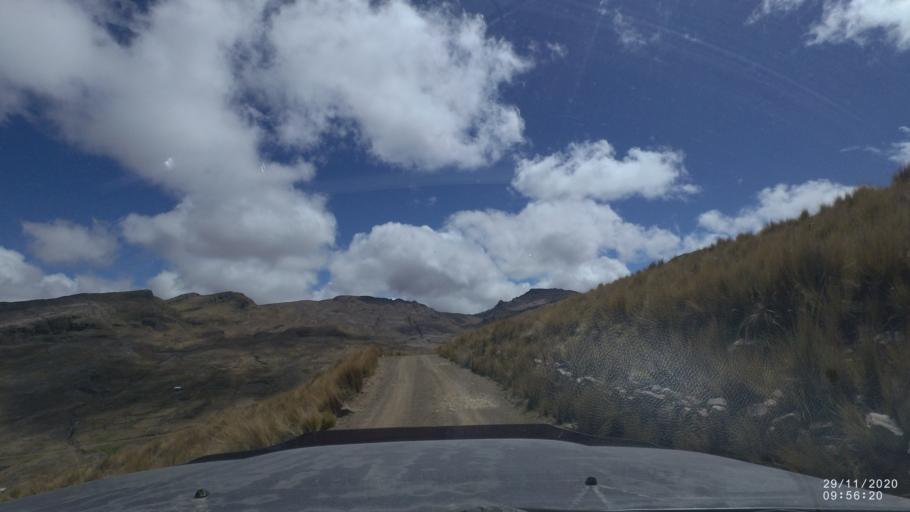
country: BO
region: Cochabamba
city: Cochabamba
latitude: -17.2718
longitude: -66.1745
